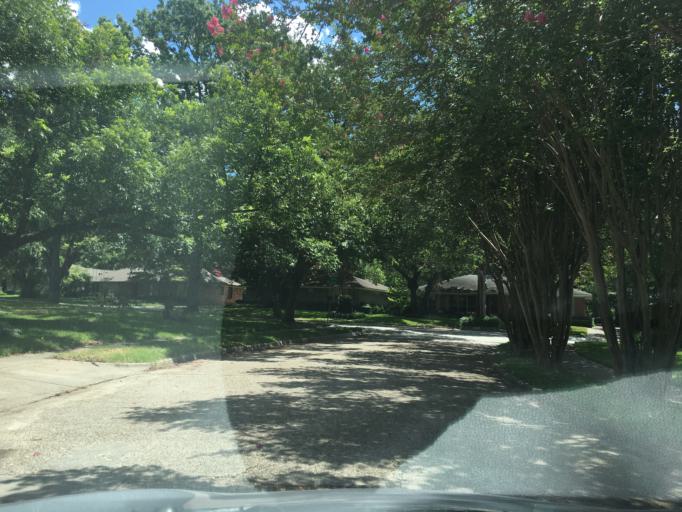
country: US
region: Texas
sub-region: Dallas County
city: Richardson
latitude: 32.8678
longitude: -96.7160
